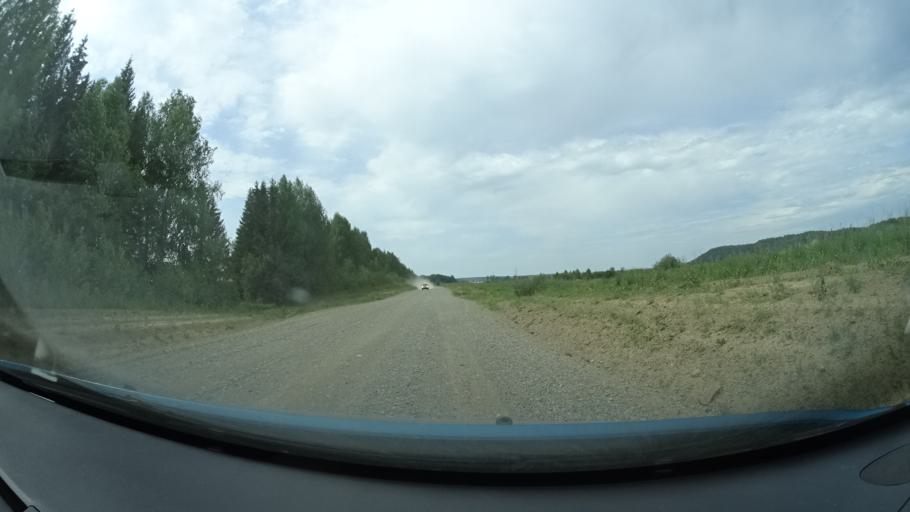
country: RU
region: Perm
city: Barda
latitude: 56.8127
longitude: 55.6519
